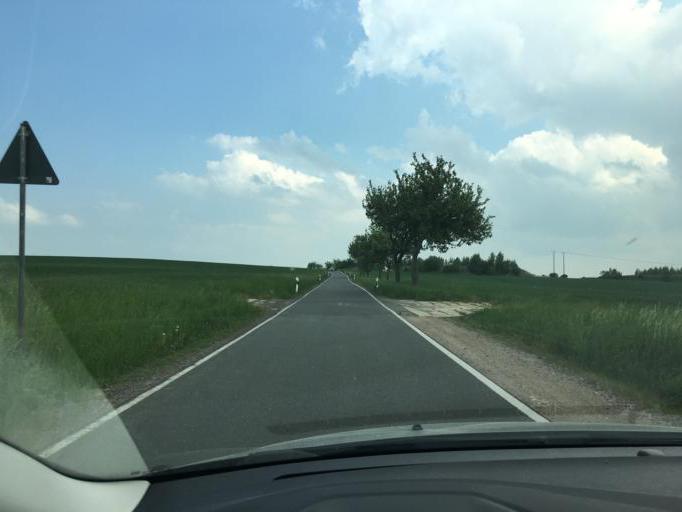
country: DE
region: Saxony
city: Rochlitz
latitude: 51.0649
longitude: 12.7993
